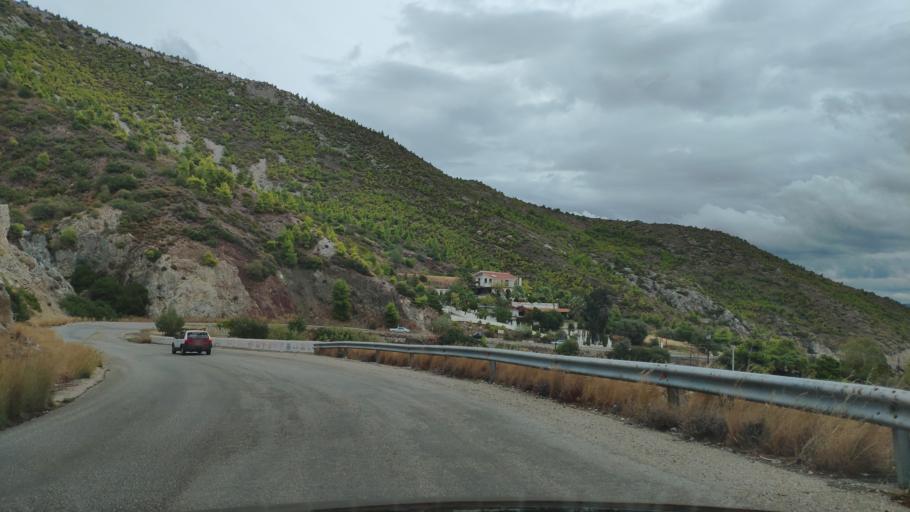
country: GR
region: Peloponnese
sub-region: Nomos Korinthias
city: Perachora
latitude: 38.0006
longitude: 22.9443
